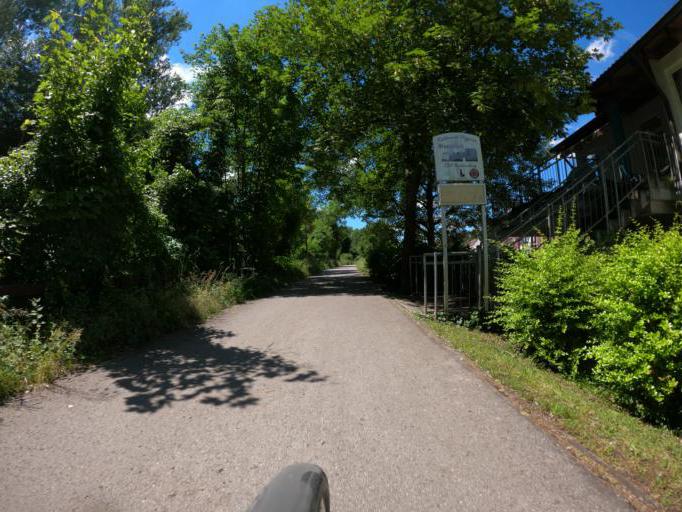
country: DE
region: Baden-Wuerttemberg
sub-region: Regierungsbezirk Stuttgart
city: Bietigheim-Bissingen
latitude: 48.9471
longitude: 9.0882
